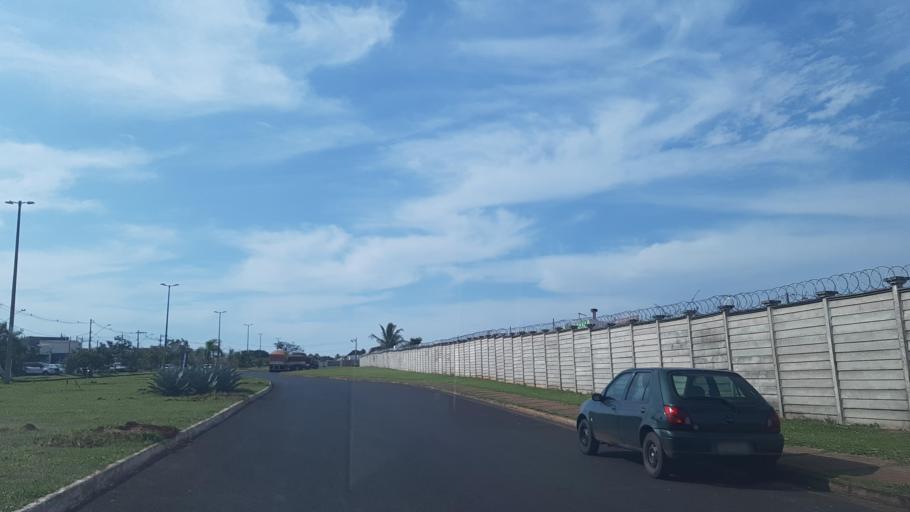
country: BR
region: Minas Gerais
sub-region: Uberlandia
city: Uberlandia
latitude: -18.8727
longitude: -48.2324
